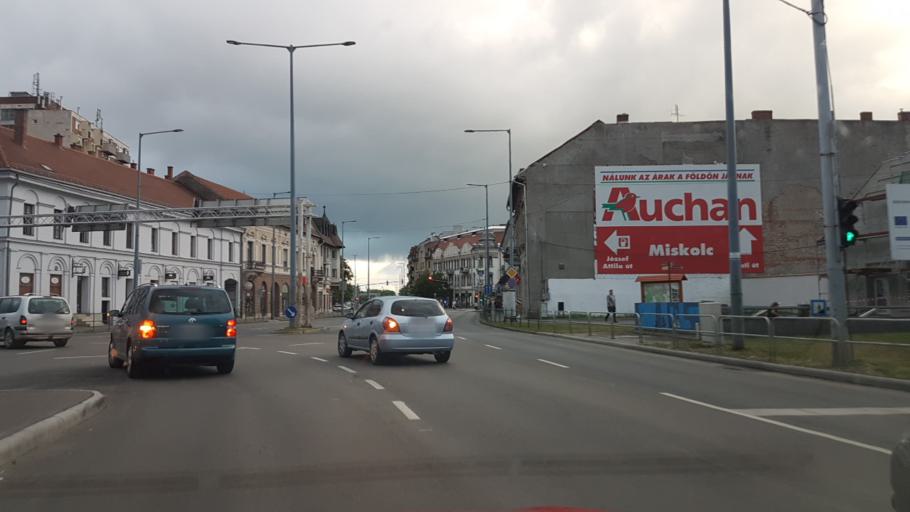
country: HU
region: Borsod-Abauj-Zemplen
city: Miskolc
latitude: 48.1044
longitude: 20.7913
